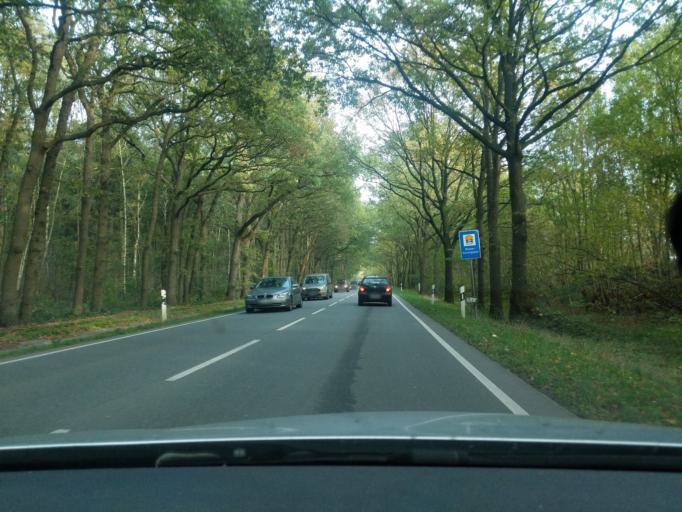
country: DE
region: Lower Saxony
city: Hammah
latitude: 53.5939
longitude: 9.4084
